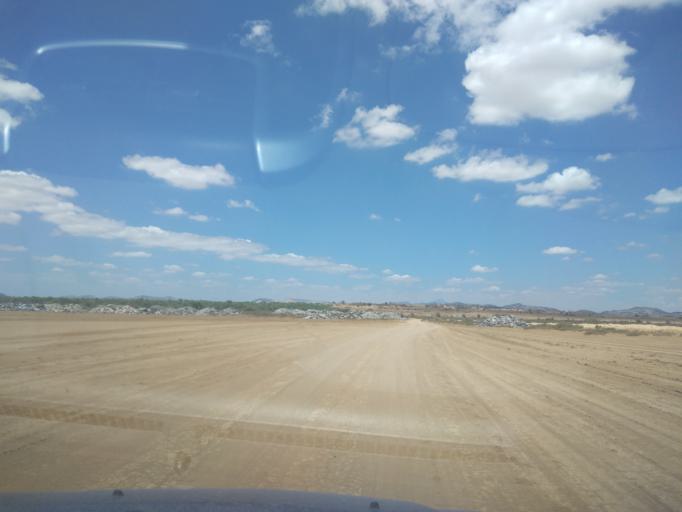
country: TN
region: Susah
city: Harqalah
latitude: 36.1641
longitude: 10.4522
